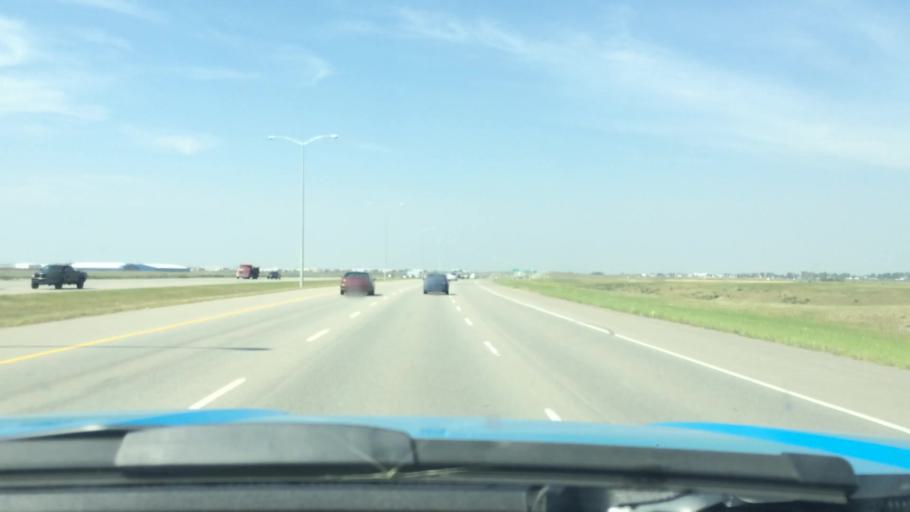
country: CA
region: Alberta
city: Chestermere
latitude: 50.9293
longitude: -113.9192
